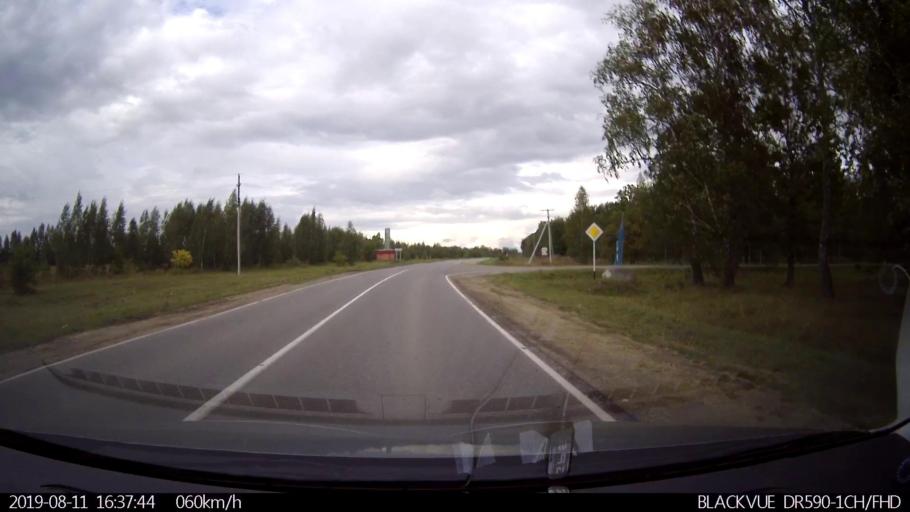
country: RU
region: Ulyanovsk
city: Mayna
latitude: 54.1298
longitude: 47.6165
